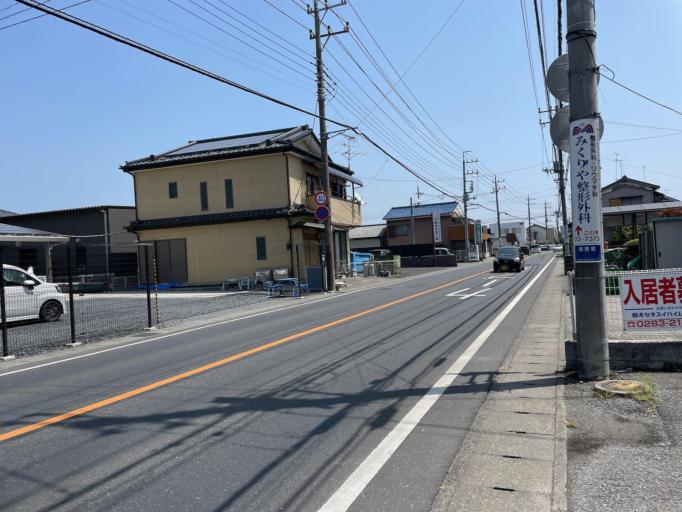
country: JP
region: Tochigi
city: Ashikaga
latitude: 36.3076
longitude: 139.4505
